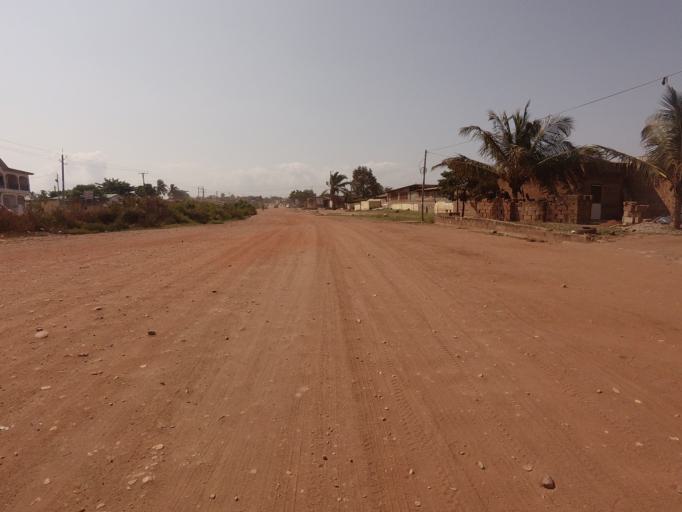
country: GH
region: Greater Accra
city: Teshi Old Town
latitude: 5.5872
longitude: -0.1148
